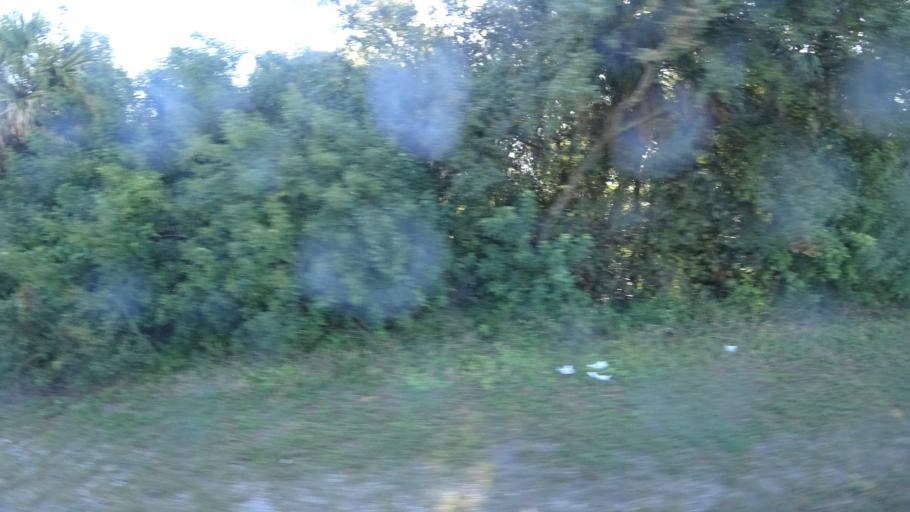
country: US
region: Florida
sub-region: Manatee County
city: Memphis
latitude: 27.6366
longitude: -82.5399
